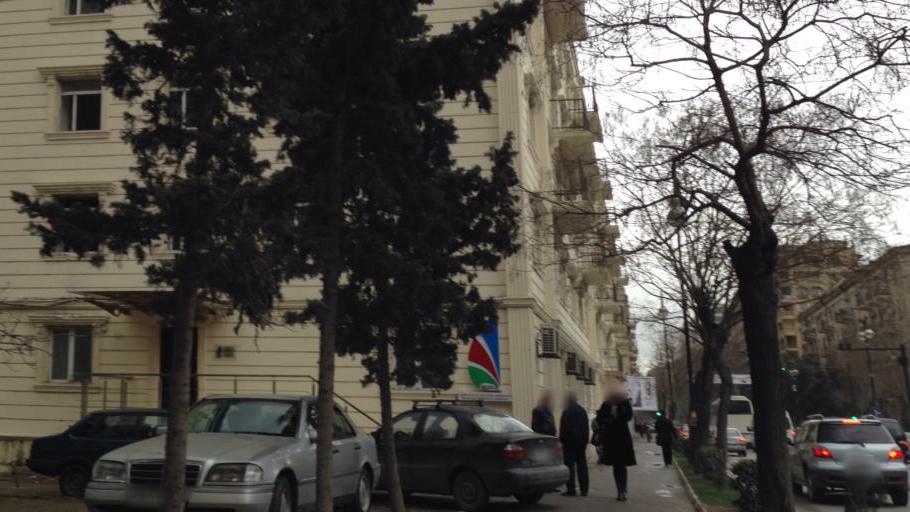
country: AZ
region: Baki
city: Baku
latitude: 40.3765
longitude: 49.8574
